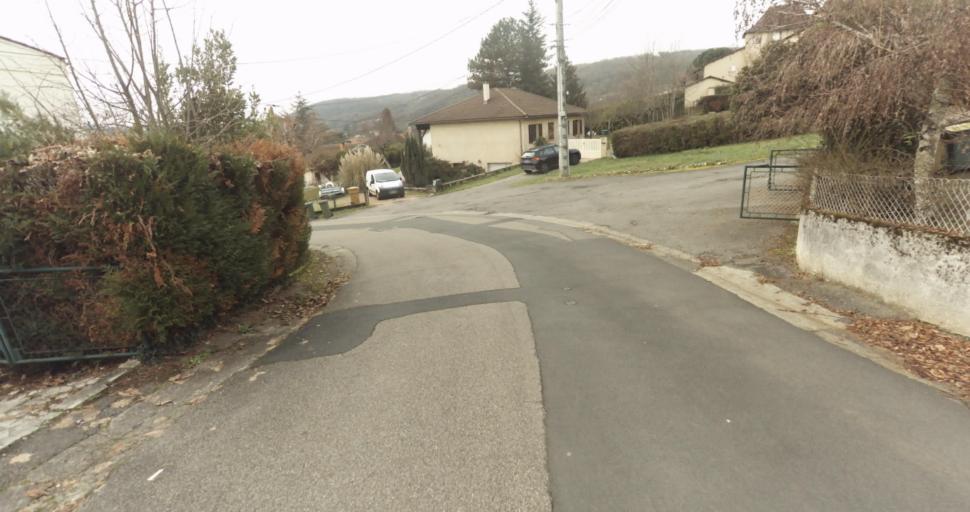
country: FR
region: Midi-Pyrenees
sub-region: Departement du Lot
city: Figeac
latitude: 44.6126
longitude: 2.0223
